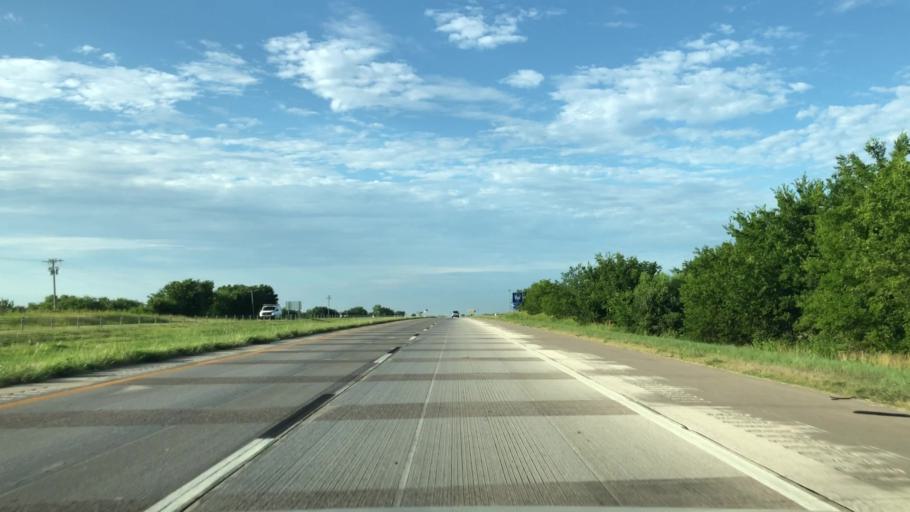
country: US
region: Oklahoma
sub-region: Osage County
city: Skiatook
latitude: 36.4271
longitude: -95.9206
